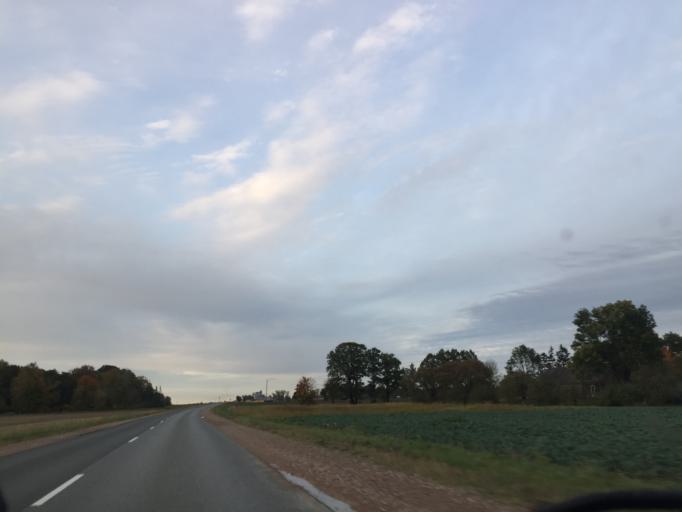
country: LV
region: Dobeles Rajons
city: Dobele
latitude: 56.7112
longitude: 23.3820
